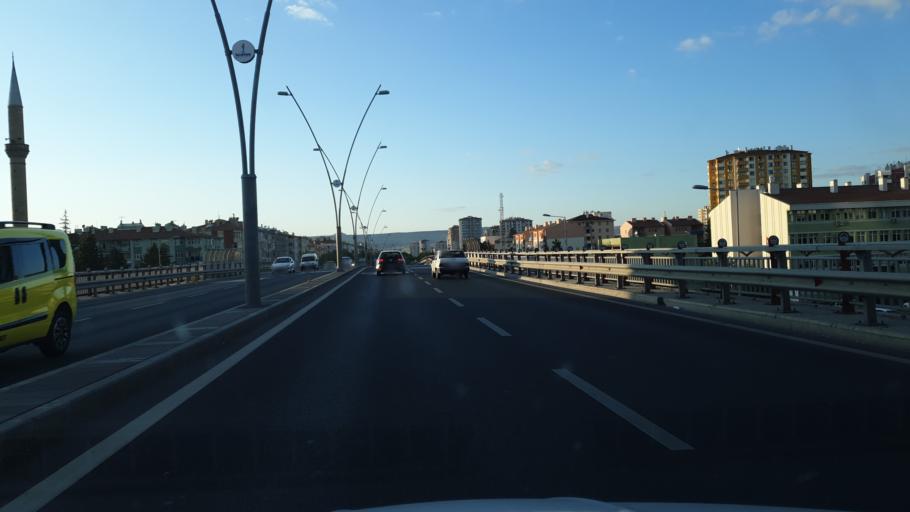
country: TR
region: Kayseri
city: Kayseri
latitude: 38.7350
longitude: 35.4934
